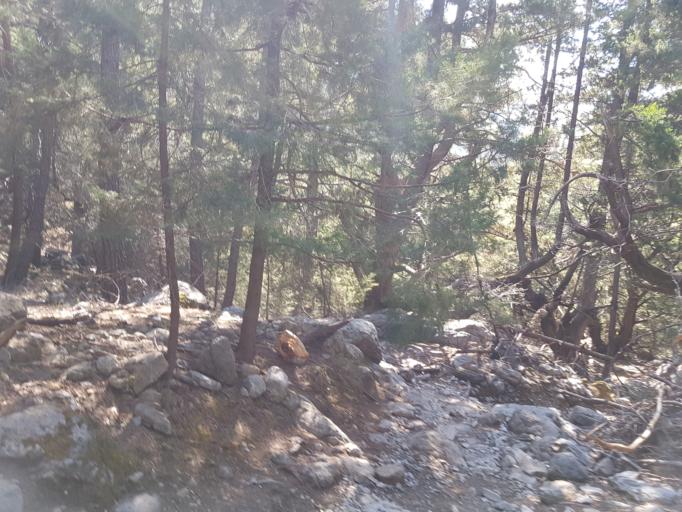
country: GR
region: Crete
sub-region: Nomos Chanias
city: Perivolia
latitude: 35.3062
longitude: 23.9369
